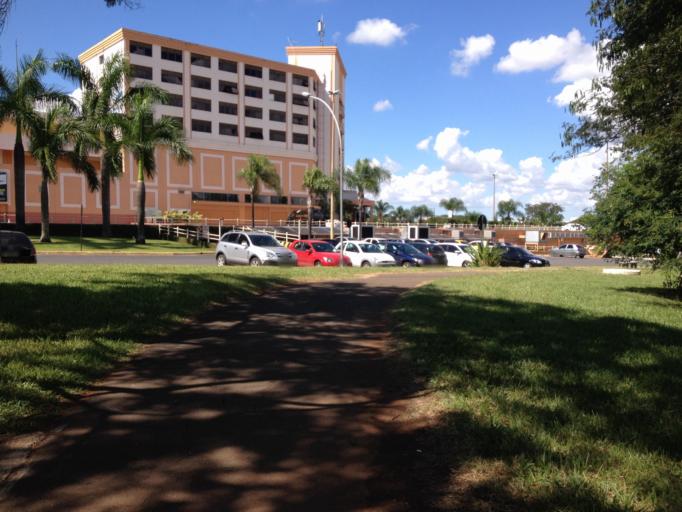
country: BR
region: Federal District
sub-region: Brasilia
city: Brasilia
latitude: -15.8023
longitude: -47.9410
